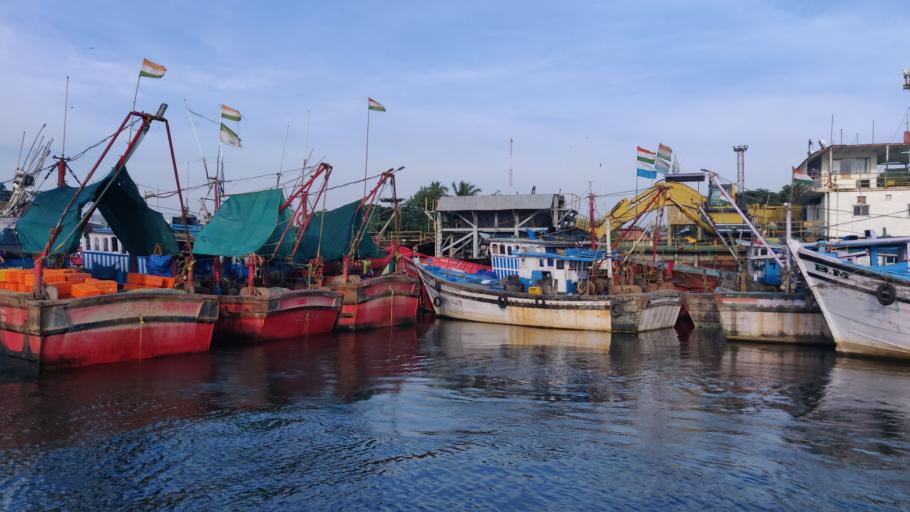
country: IN
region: Karnataka
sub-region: Dakshina Kannada
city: Ullal
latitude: 12.8620
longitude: 74.8309
